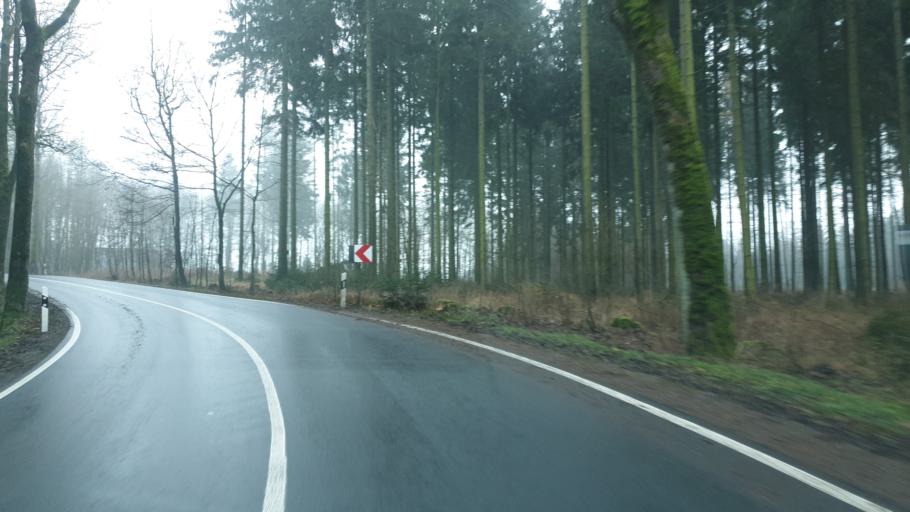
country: DE
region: Saxony
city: Neuhausen
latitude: 50.6953
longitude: 13.4527
